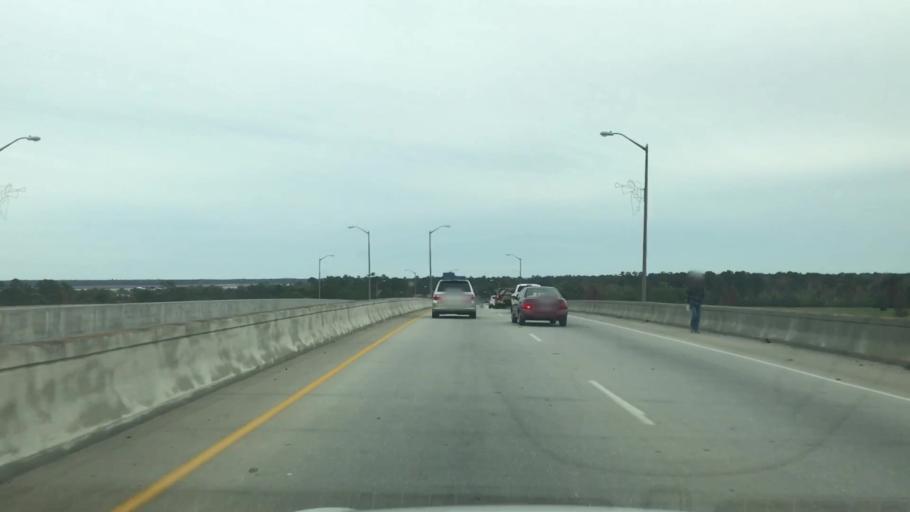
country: US
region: South Carolina
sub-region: Georgetown County
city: Georgetown
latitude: 33.3582
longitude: -79.2944
